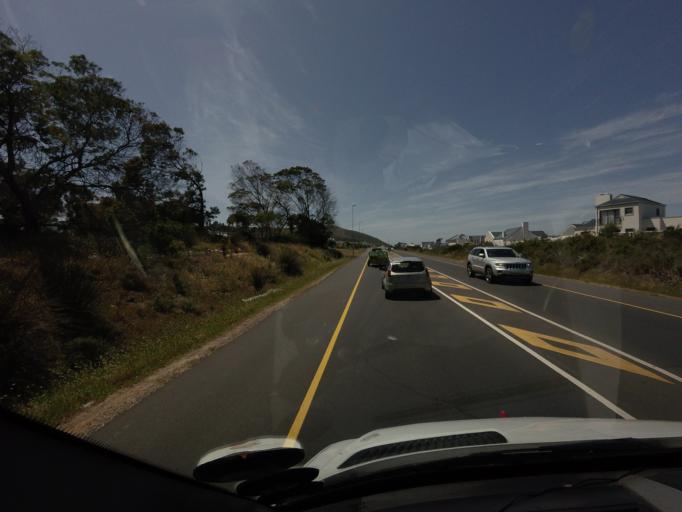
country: ZA
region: Western Cape
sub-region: Overberg District Municipality
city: Hermanus
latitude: -34.4110
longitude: 19.1956
